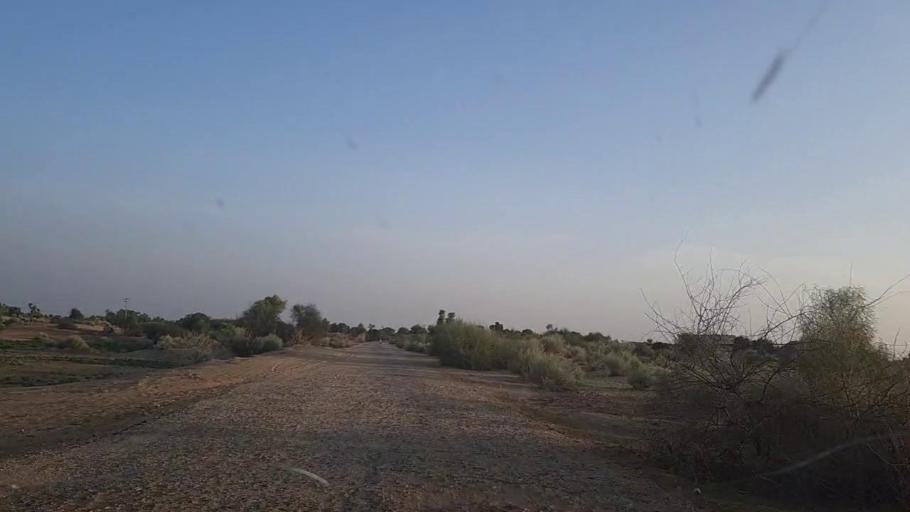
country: PK
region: Sindh
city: Khanpur
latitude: 27.6283
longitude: 69.4445
